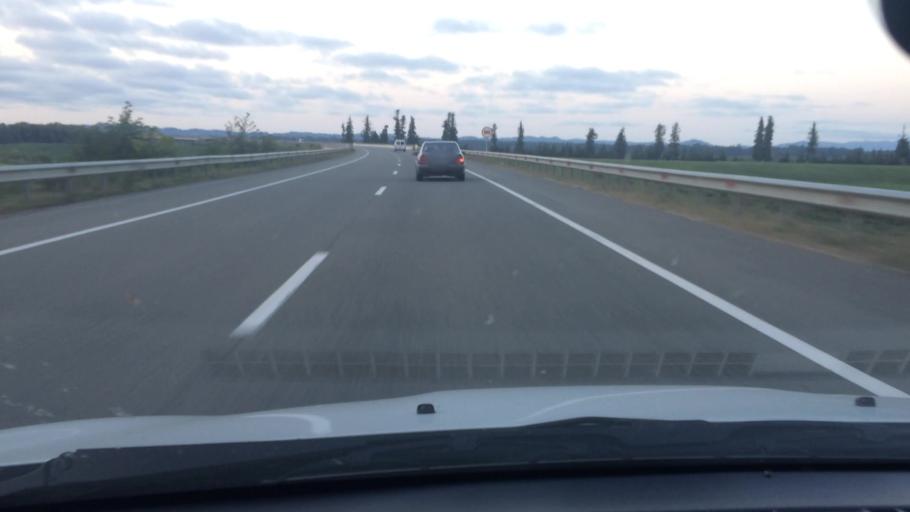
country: GE
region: Ajaria
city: Ochkhamuri
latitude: 41.8574
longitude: 41.8384
